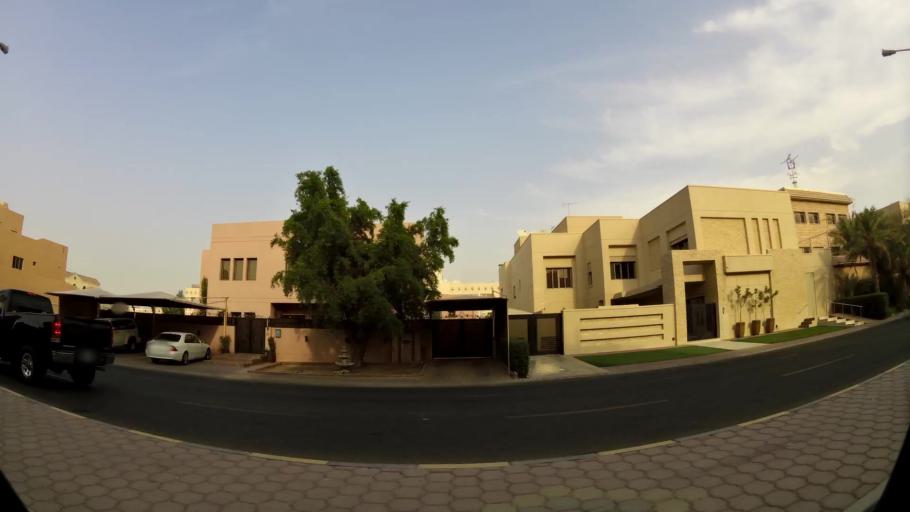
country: KW
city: Bayan
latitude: 29.3115
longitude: 48.0328
